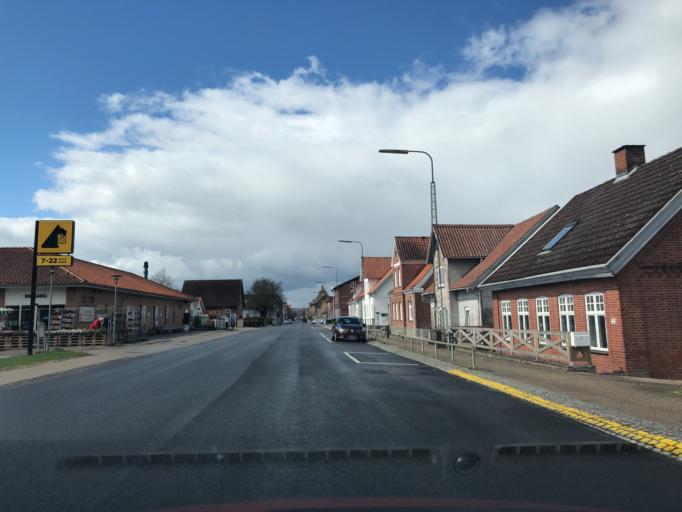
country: DK
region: South Denmark
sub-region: Kolding Kommune
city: Christiansfeld
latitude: 55.3557
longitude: 9.4889
